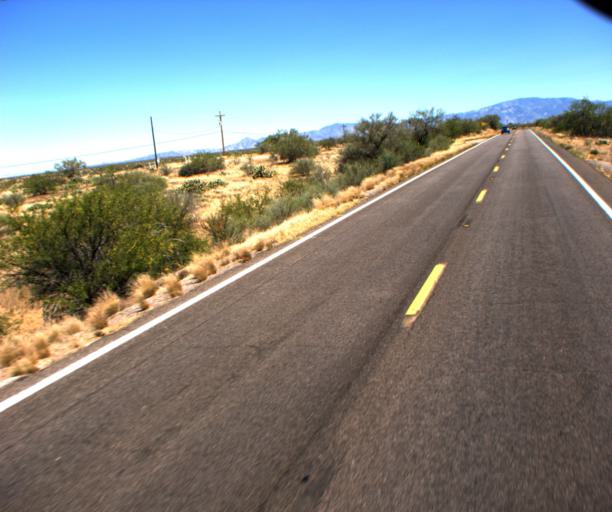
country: US
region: Arizona
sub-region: Pima County
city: Catalina
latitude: 32.6374
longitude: -111.0107
